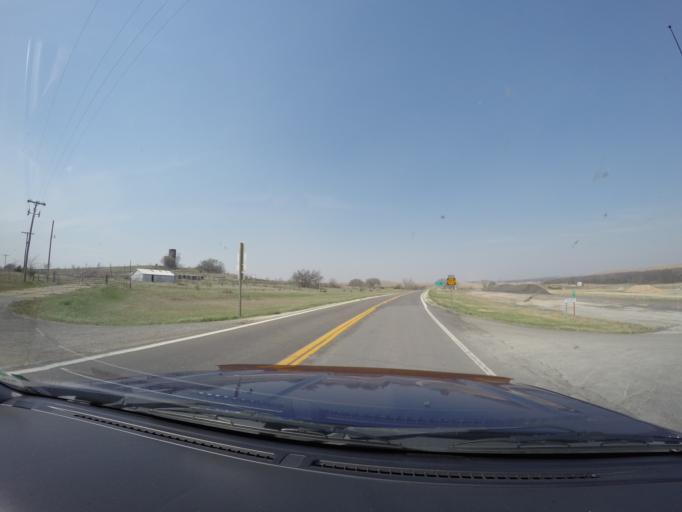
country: US
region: Kansas
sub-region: Chase County
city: Cottonwood Falls
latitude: 38.4019
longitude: -96.5553
